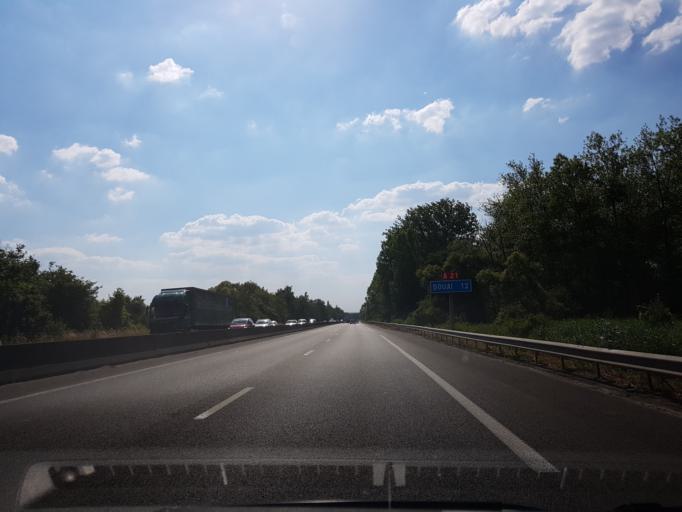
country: FR
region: Nord-Pas-de-Calais
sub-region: Departement du Nord
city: Pecquencourt
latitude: 50.3829
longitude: 3.2123
